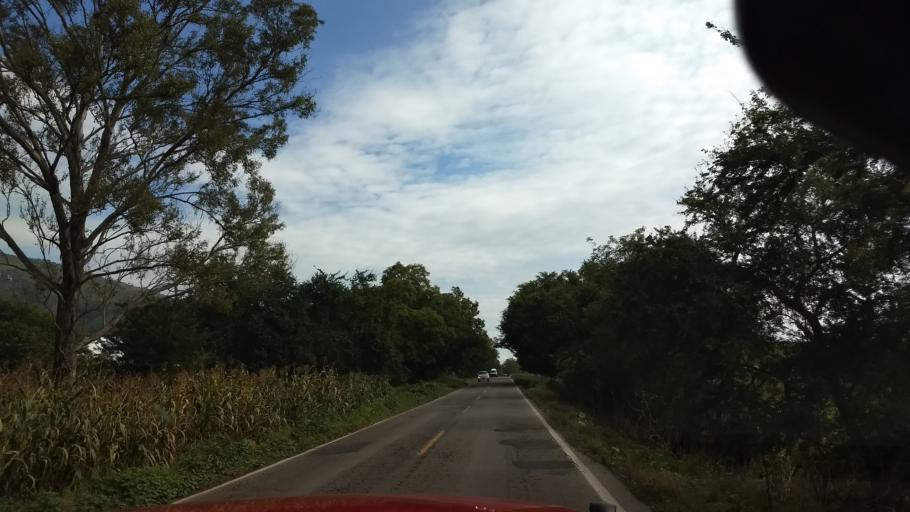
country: MX
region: Jalisco
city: Tuxpan
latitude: 19.5414
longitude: -103.4060
